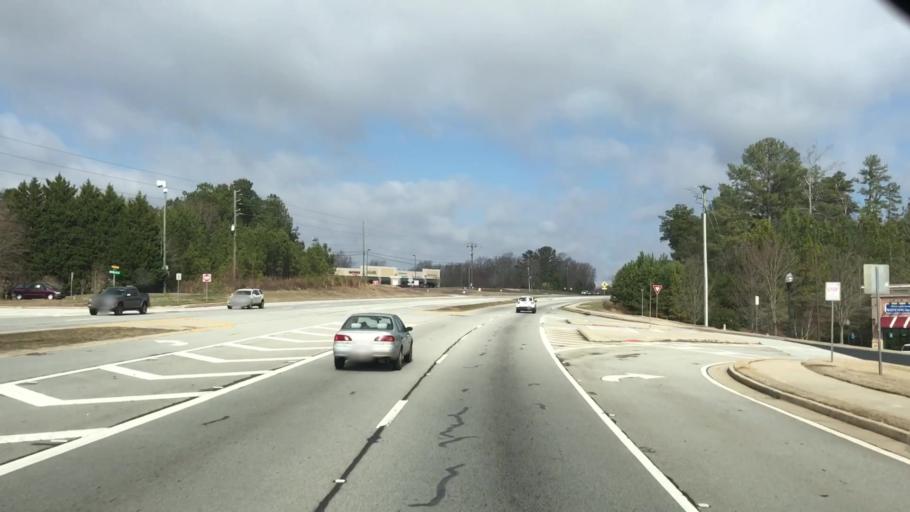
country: US
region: Georgia
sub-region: Hall County
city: Oakwood
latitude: 34.1980
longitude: -83.8589
